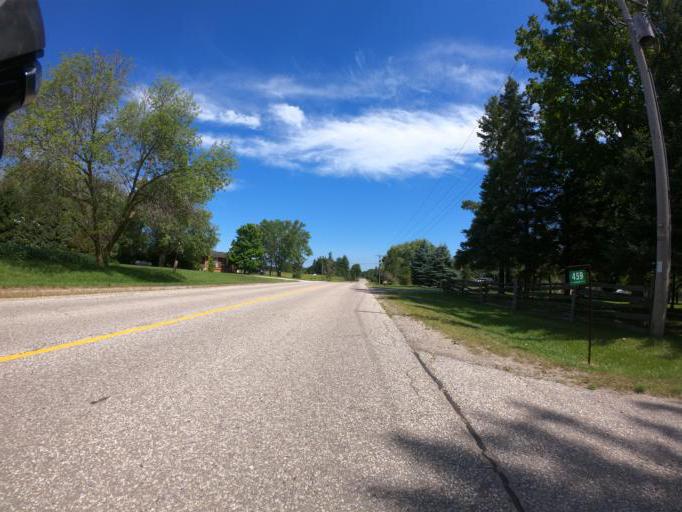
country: CA
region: Ontario
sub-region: Wellington County
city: Guelph
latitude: 43.5536
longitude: -80.3767
